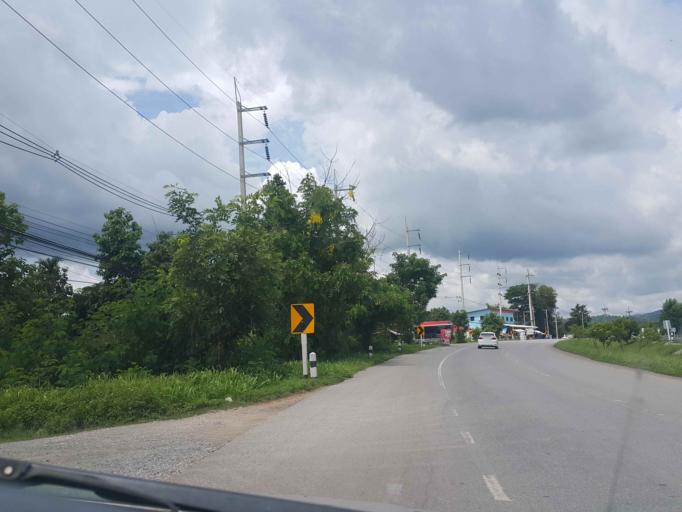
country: TH
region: Phayao
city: Dok Kham Tai
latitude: 19.0206
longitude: 99.9202
